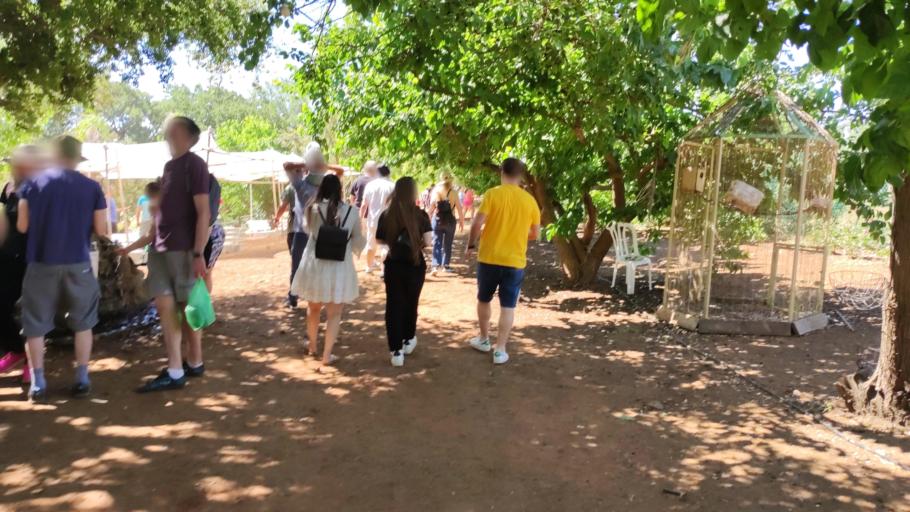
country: SY
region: Quneitra
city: Al Qunaytirah
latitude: 33.1177
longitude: 35.8058
